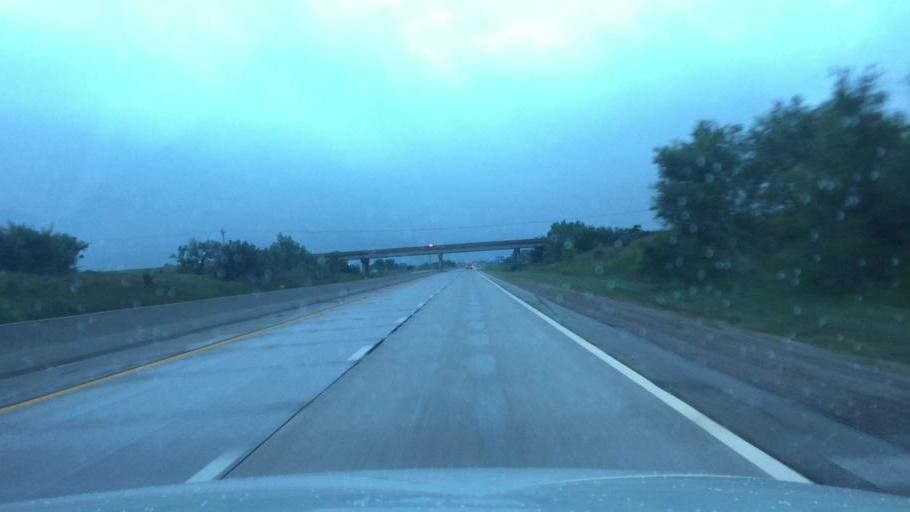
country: US
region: Kansas
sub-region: Neosho County
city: Chanute
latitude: 37.6621
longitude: -95.4796
